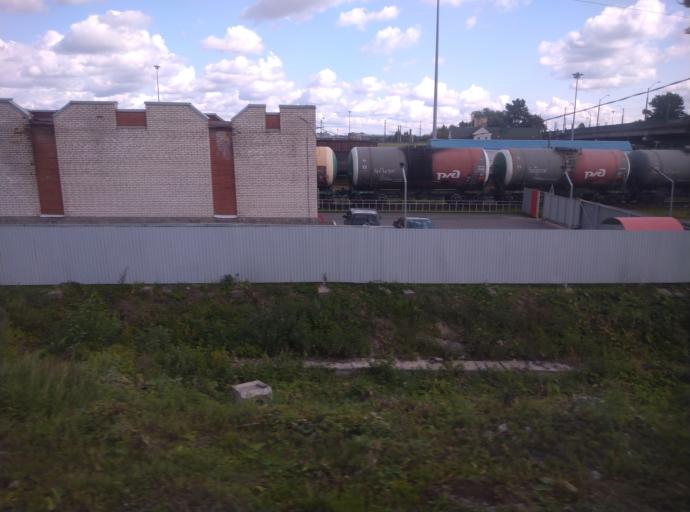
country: RU
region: St.-Petersburg
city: Obukhovo
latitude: 59.8689
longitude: 30.4217
